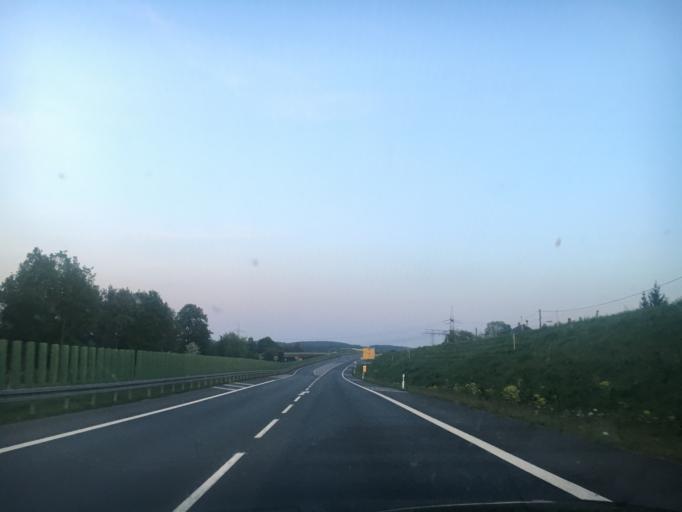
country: DE
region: Thuringia
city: Crimla
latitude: 50.8286
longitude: 12.0736
